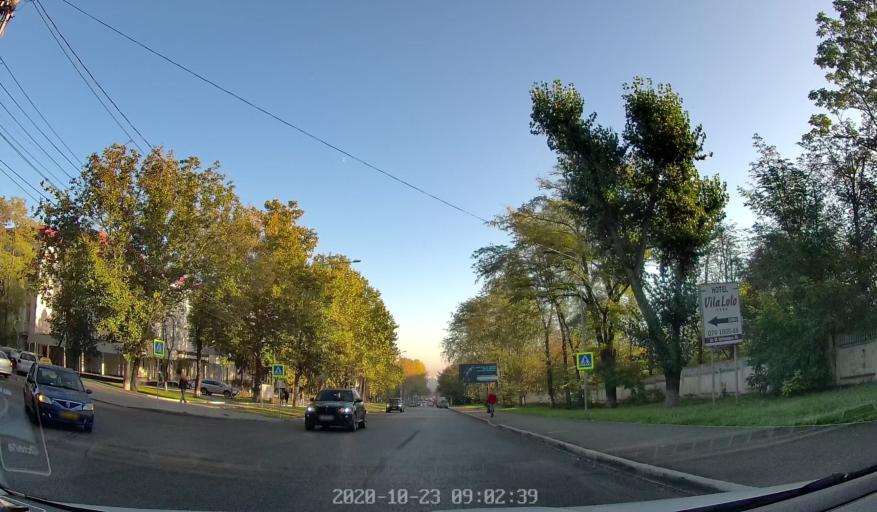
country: MD
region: Chisinau
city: Chisinau
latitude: 46.9925
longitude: 28.8295
